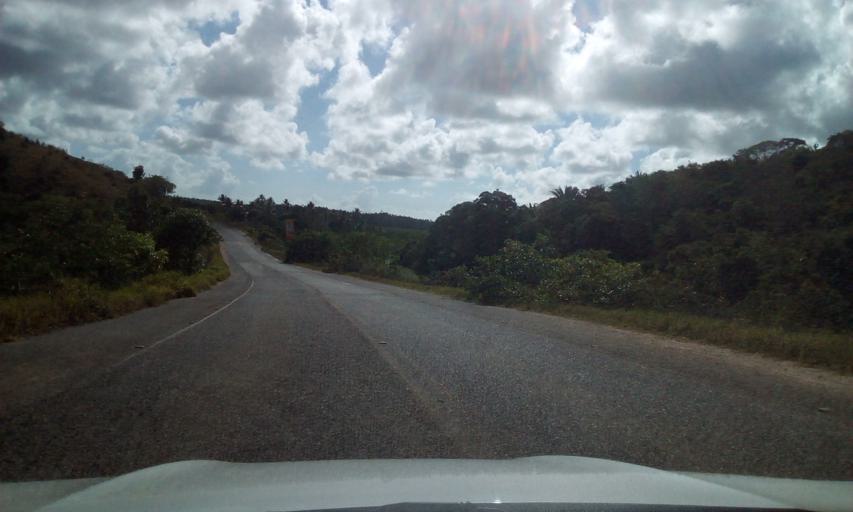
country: BR
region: Sergipe
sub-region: Indiaroba
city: Indiaroba
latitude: -11.5362
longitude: -37.5586
